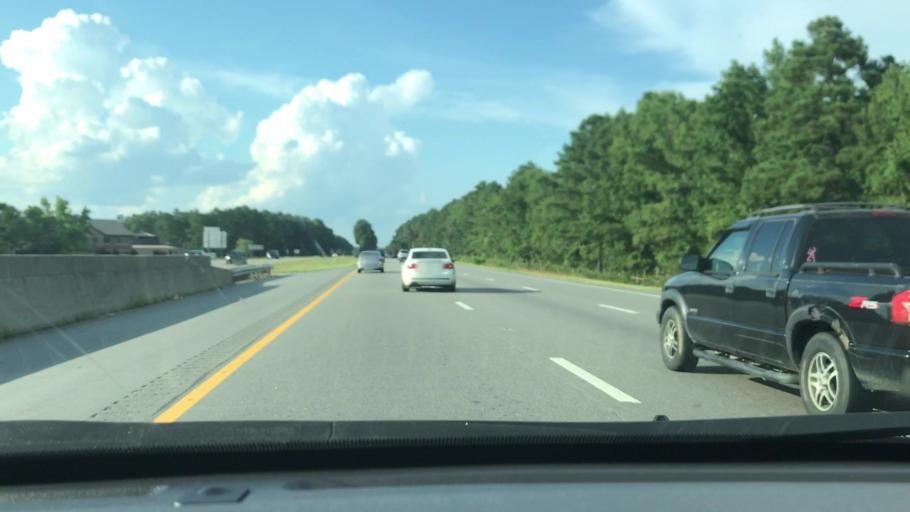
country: US
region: North Carolina
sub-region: Robeson County
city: Lumberton
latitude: 34.6742
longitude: -79.0042
